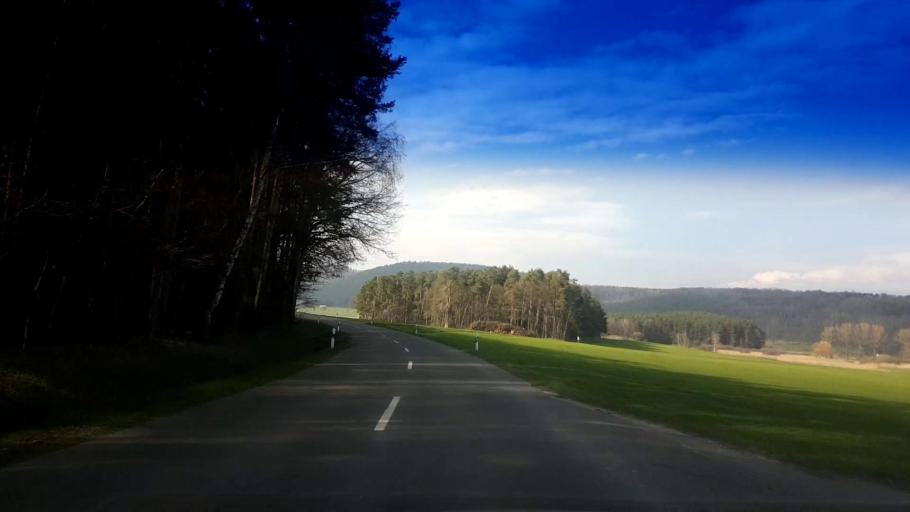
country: DE
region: Bavaria
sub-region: Upper Franconia
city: Trebgast
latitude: 50.0459
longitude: 11.5325
